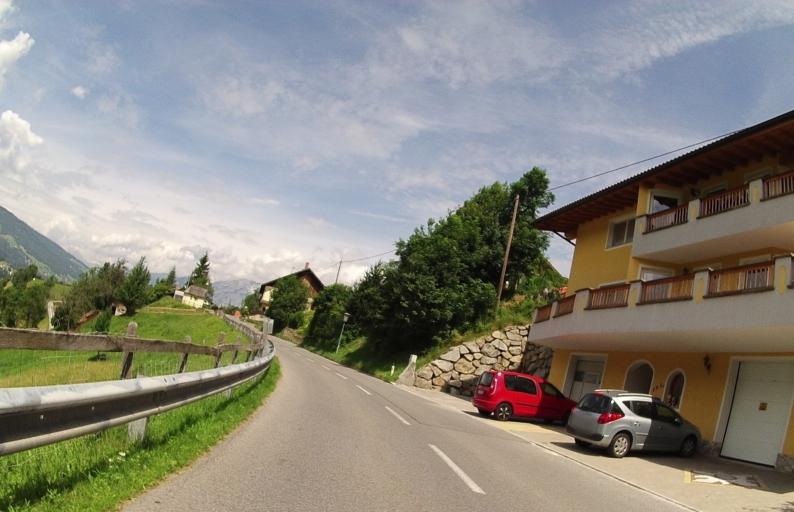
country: AT
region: Tyrol
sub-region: Politischer Bezirk Innsbruck Land
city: Ellbogen
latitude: 47.1770
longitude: 11.4393
